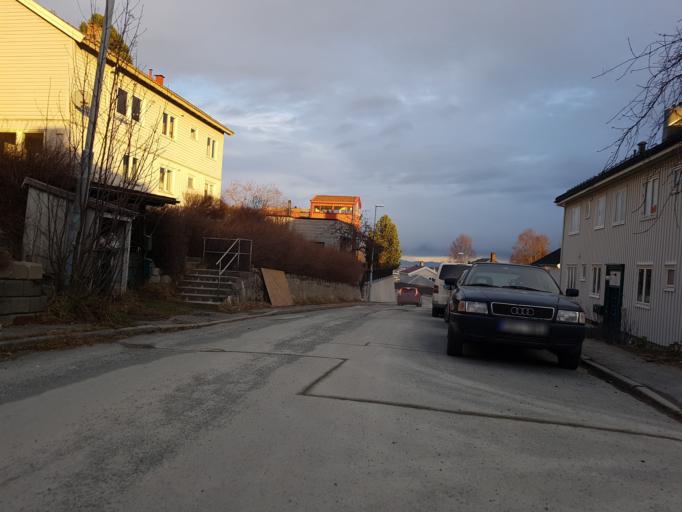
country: NO
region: Sor-Trondelag
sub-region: Trondheim
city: Trondheim
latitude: 63.4176
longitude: 10.3700
